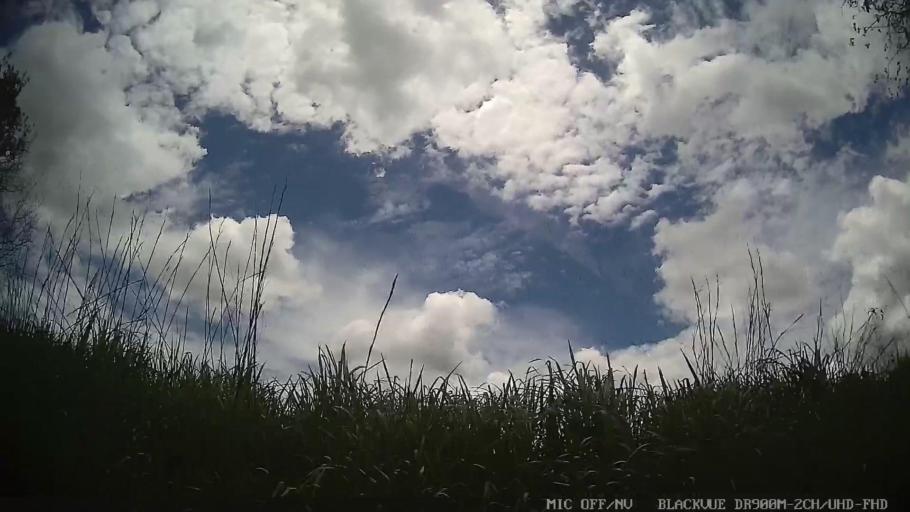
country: BR
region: Sao Paulo
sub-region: Jaguariuna
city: Jaguariuna
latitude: -22.7580
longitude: -47.0054
